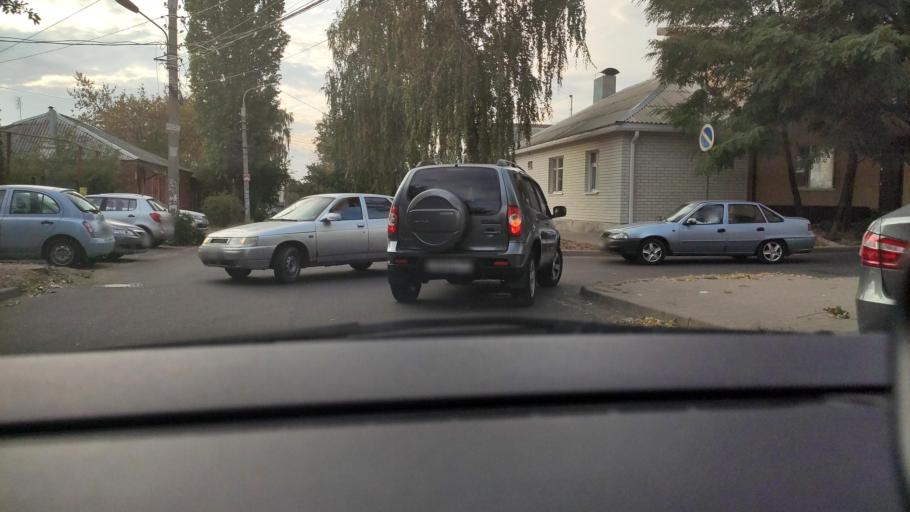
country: RU
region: Voronezj
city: Voronezh
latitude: 51.6851
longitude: 39.2135
